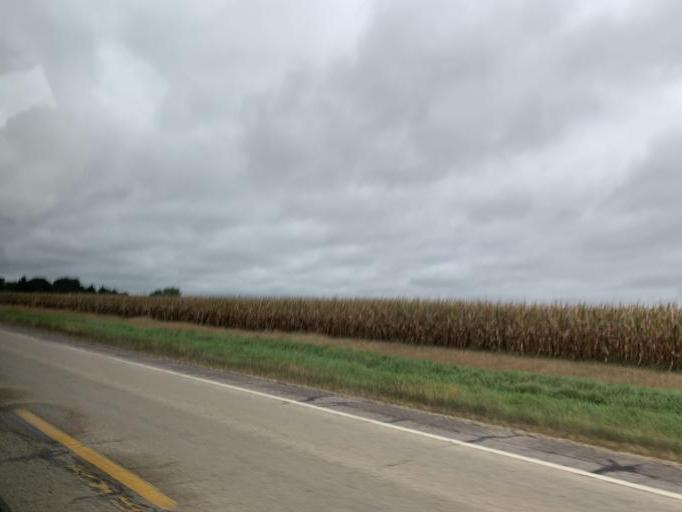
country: US
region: Wisconsin
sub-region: Sauk County
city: Sauk City
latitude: 43.2710
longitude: -89.7825
